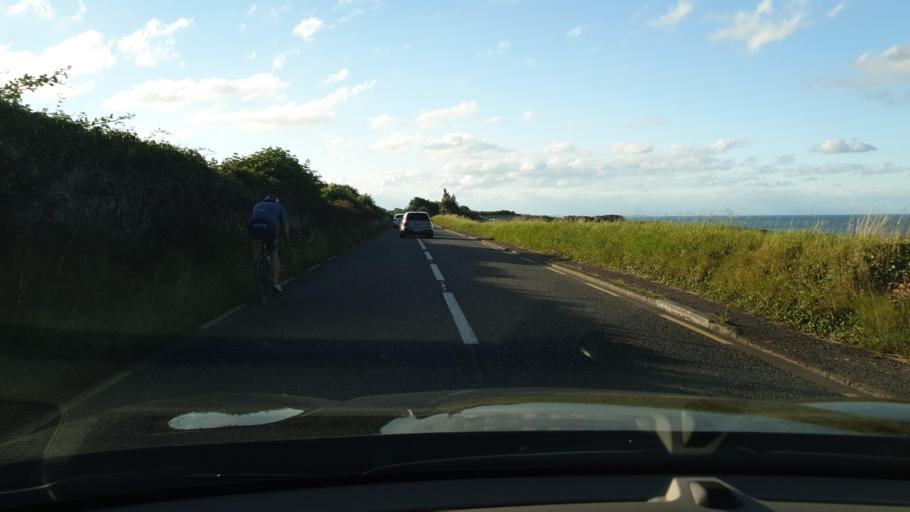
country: IE
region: Leinster
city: Balrothery
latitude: 53.5948
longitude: -6.1598
